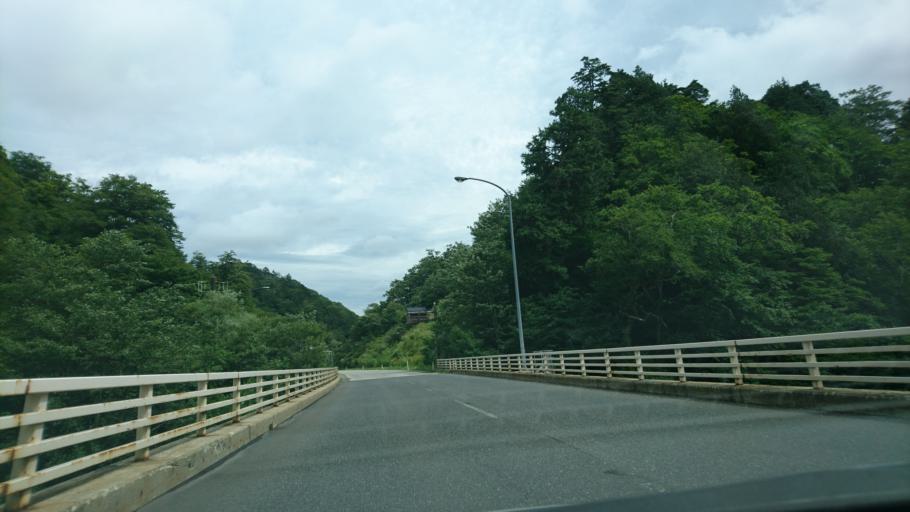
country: JP
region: Yamagata
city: Shinjo
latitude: 38.8546
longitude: 140.5971
